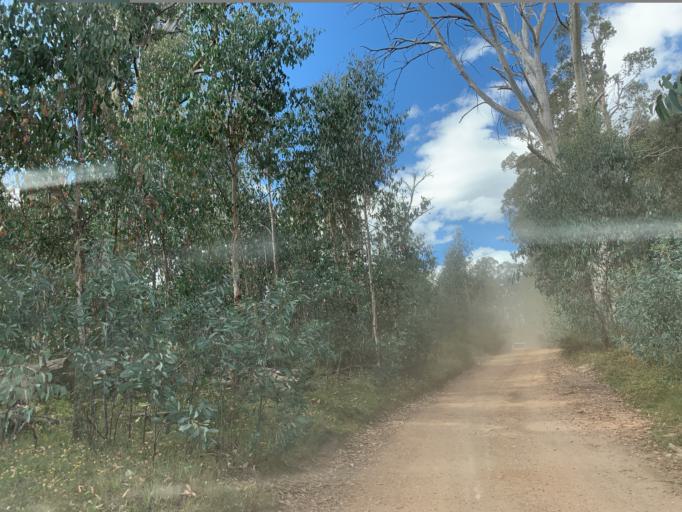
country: AU
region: Victoria
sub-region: Mansfield
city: Mansfield
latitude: -37.1017
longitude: 146.5432
